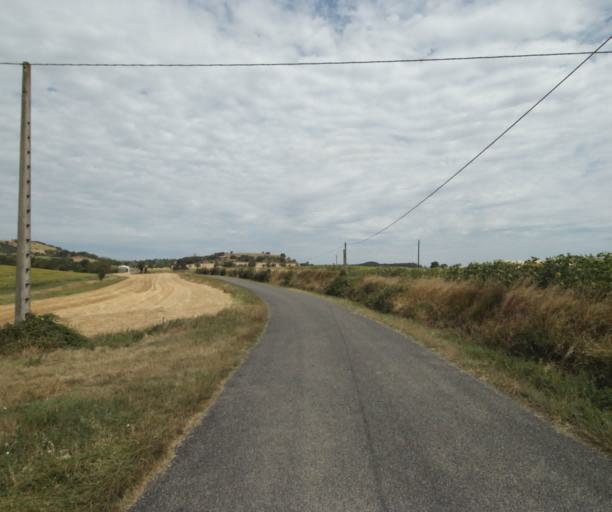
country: FR
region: Midi-Pyrenees
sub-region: Departement de la Haute-Garonne
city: Saint-Felix-Lauragais
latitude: 43.4297
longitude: 1.8987
